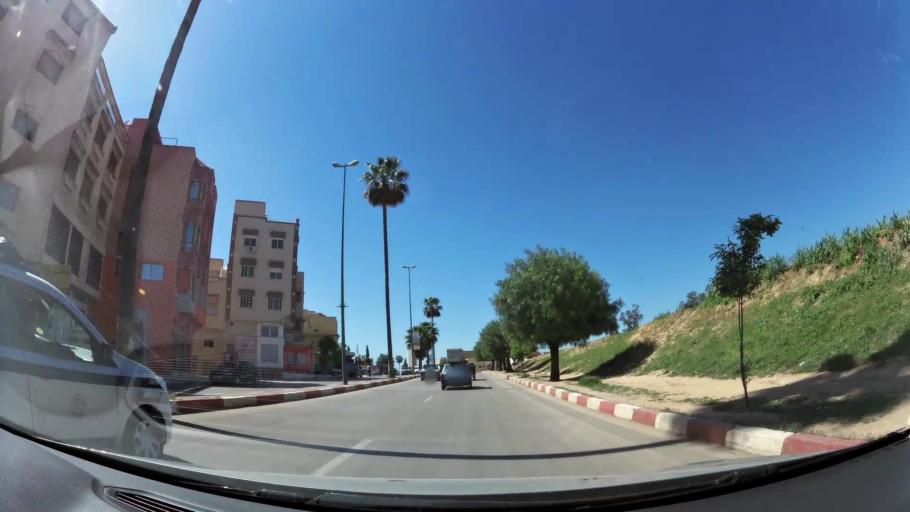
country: MA
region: Meknes-Tafilalet
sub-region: Meknes
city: Meknes
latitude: 33.8760
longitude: -5.5597
